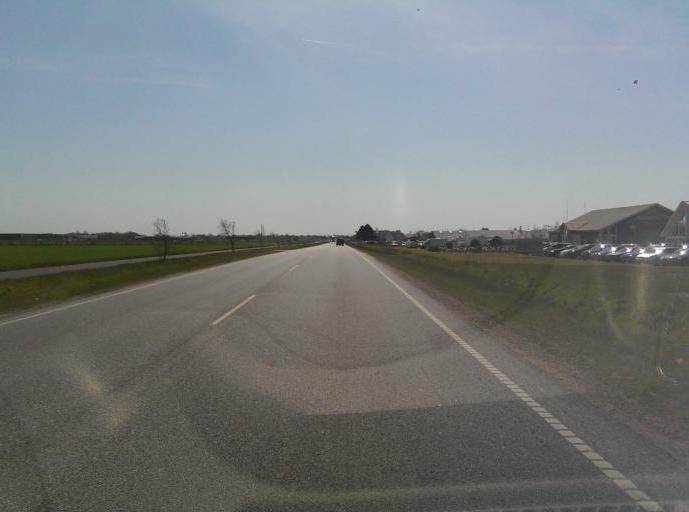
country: DK
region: South Denmark
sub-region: Esbjerg Kommune
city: Ribe
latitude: 55.3586
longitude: 8.7738
